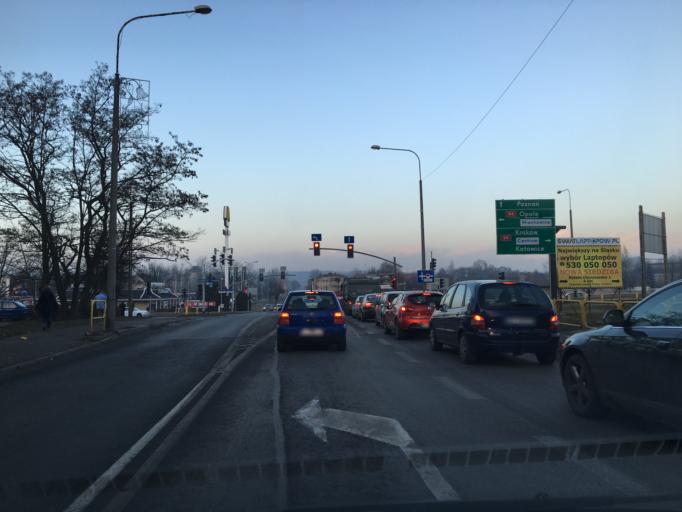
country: PL
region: Silesian Voivodeship
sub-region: Powiat tarnogorski
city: Radzionkow
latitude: 50.3522
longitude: 18.8765
